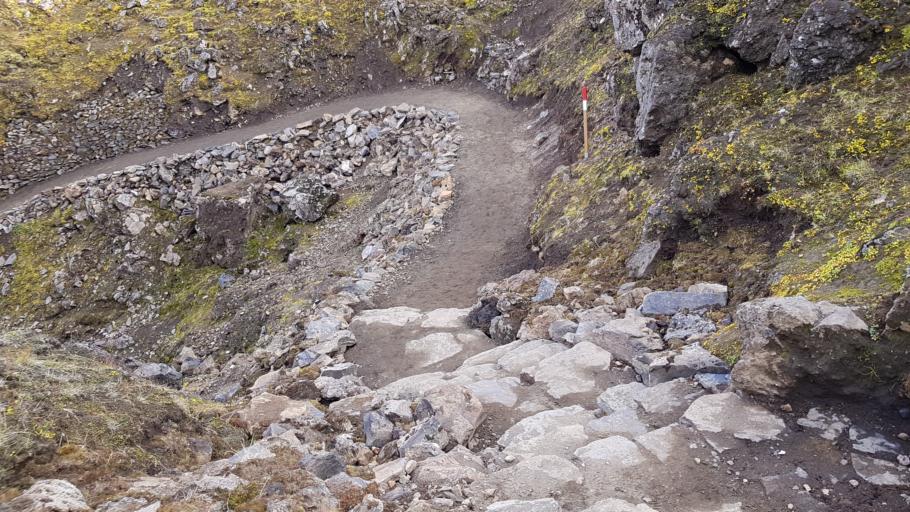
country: IS
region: South
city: Vestmannaeyjar
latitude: 63.9908
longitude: -19.0648
